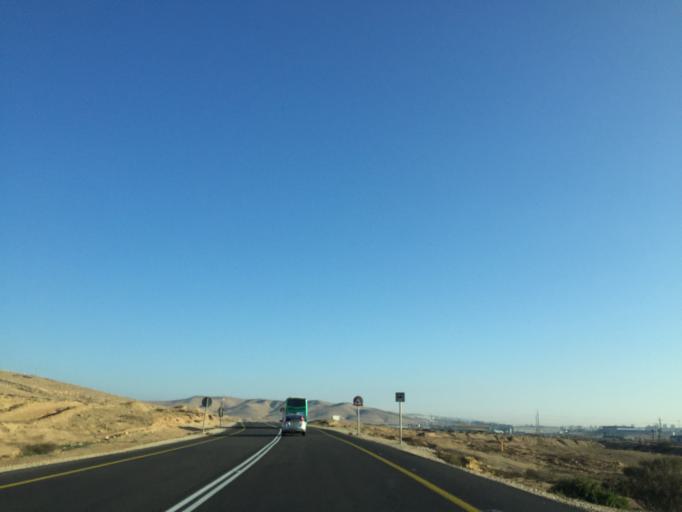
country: IL
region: Southern District
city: Dimona
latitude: 31.0541
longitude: 34.9973
